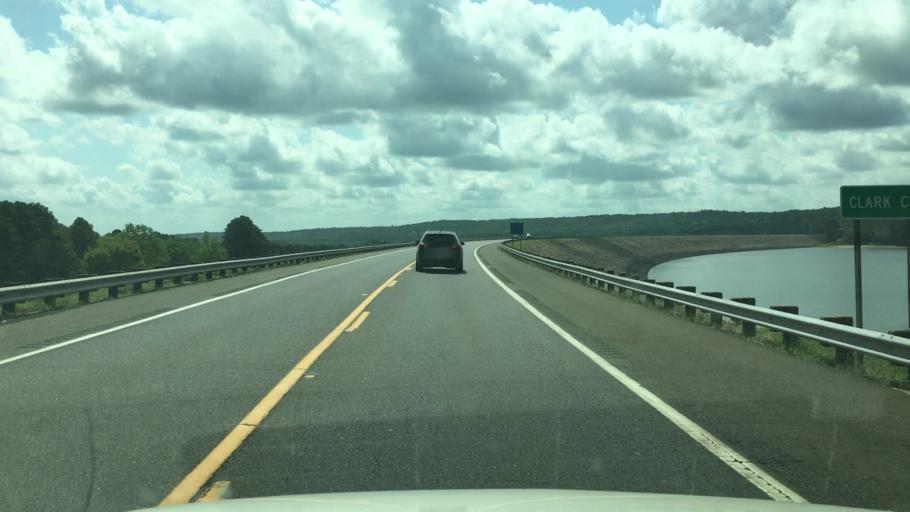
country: US
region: Arkansas
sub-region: Clark County
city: Arkadelphia
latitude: 34.2461
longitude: -93.1107
